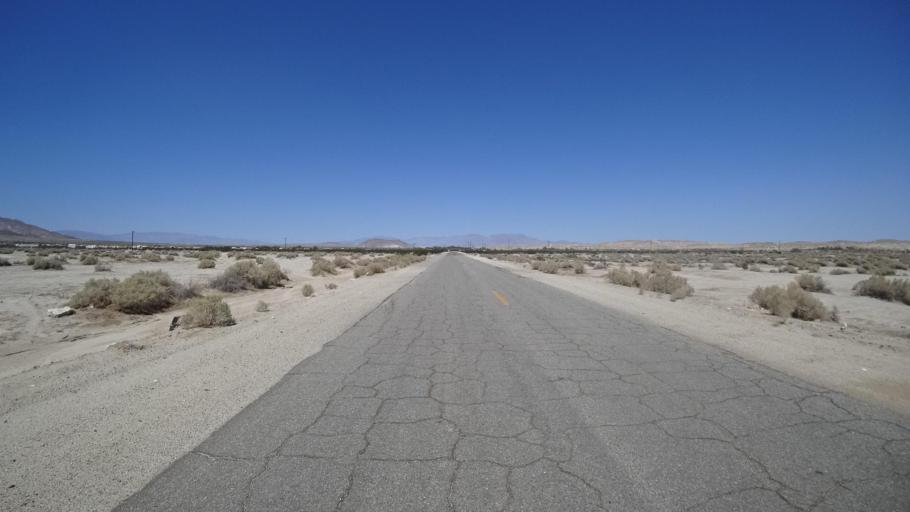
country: US
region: California
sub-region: Imperial County
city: Salton City
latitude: 33.0955
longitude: -116.1136
